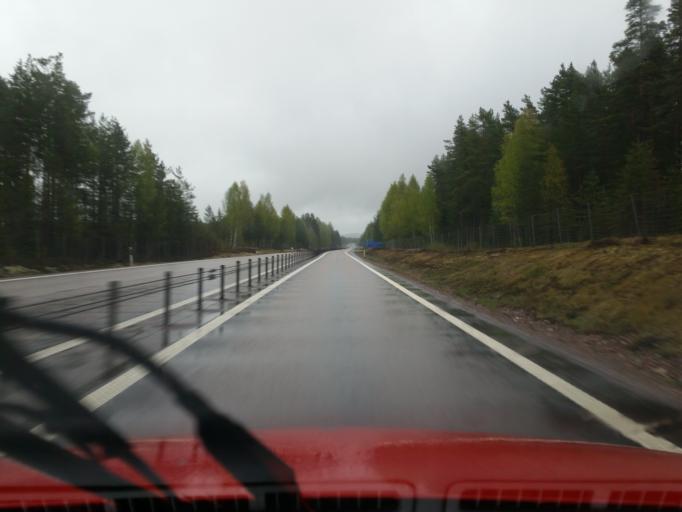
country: SE
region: Dalarna
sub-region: Saters Kommun
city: Saeter
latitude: 60.3857
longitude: 15.6538
